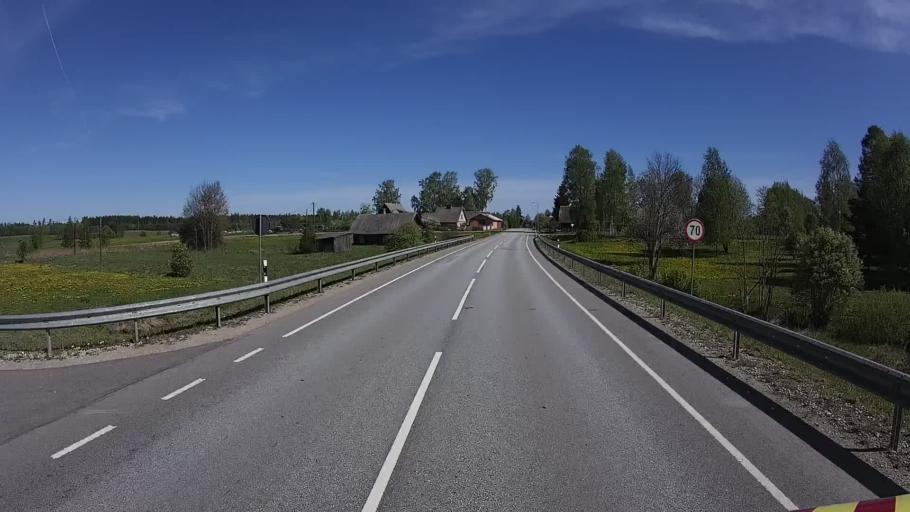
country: RU
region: Pskov
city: Pechory
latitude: 57.9365
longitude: 27.5772
